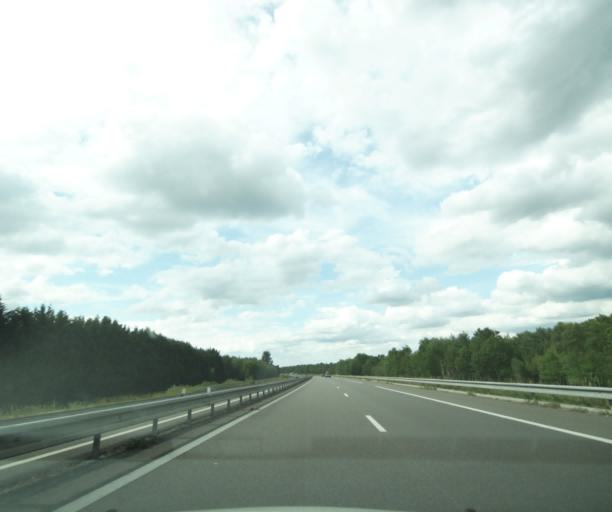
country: FR
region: Centre
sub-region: Departement du Loir-et-Cher
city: Salbris
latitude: 47.3868
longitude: 2.0485
